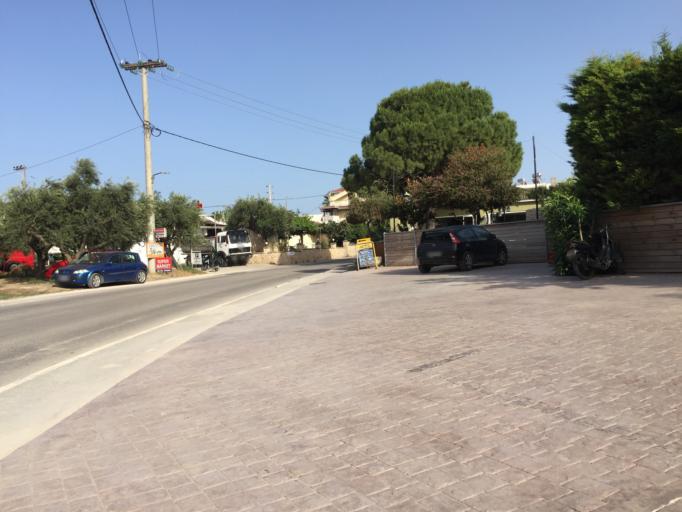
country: GR
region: Ionian Islands
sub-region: Nomos Zakynthou
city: Vanaton
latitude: 37.8189
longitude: 20.8616
